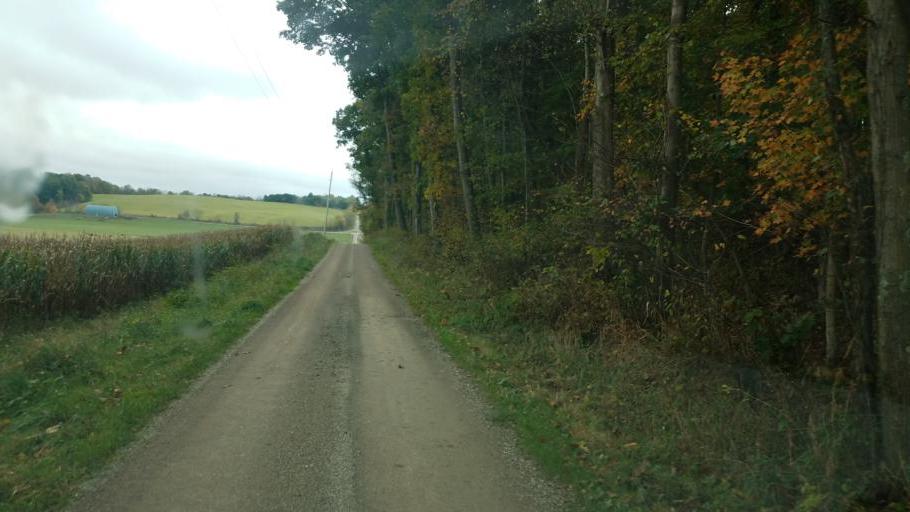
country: US
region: Ohio
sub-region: Ashland County
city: Loudonville
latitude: 40.6031
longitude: -82.1772
